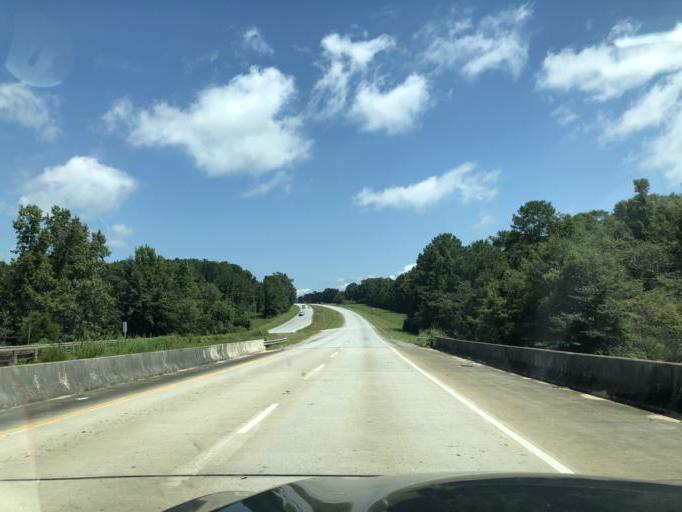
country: US
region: Alabama
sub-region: Barbour County
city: Eufaula
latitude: 31.7720
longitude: -85.1843
